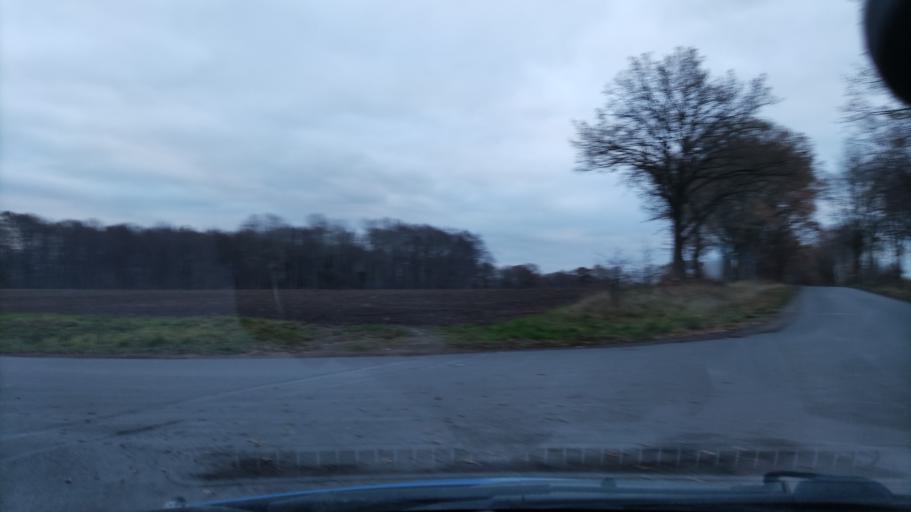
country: DE
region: Lower Saxony
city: Reppenstedt
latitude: 53.2588
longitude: 10.3536
